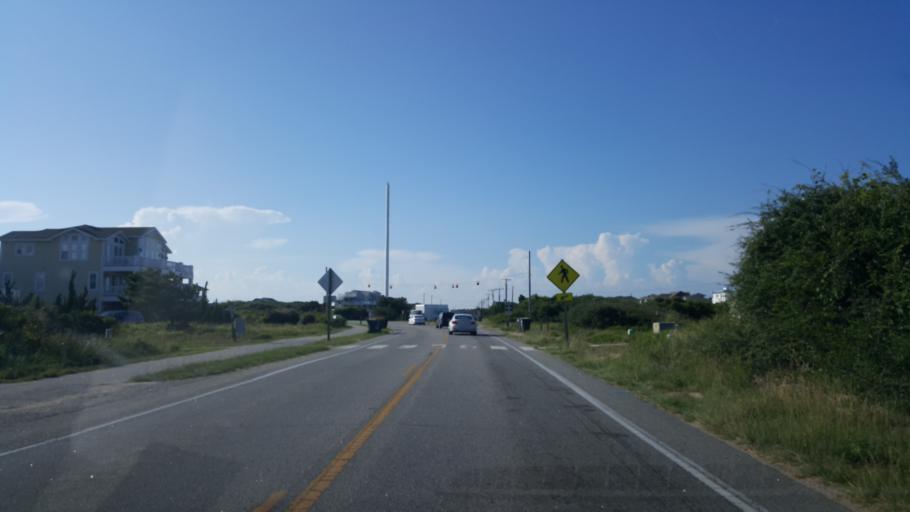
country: US
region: North Carolina
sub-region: Dare County
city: Southern Shores
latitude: 36.1193
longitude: -75.7226
